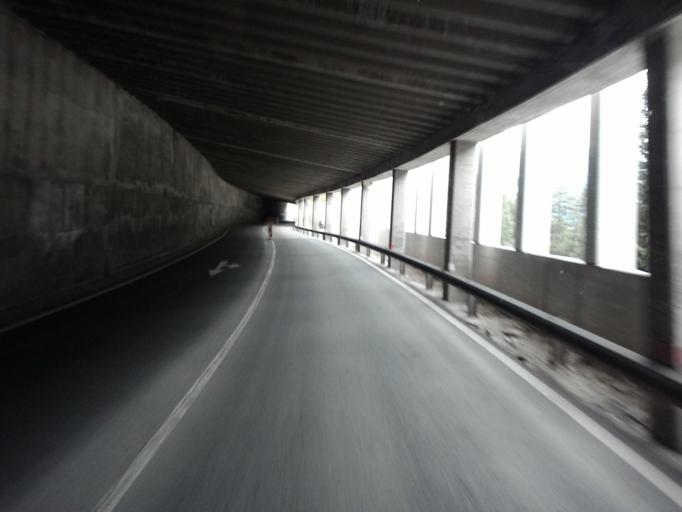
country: AT
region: Tyrol
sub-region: Politischer Bezirk Lienz
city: Matrei in Osttirol
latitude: 47.0768
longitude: 12.5309
